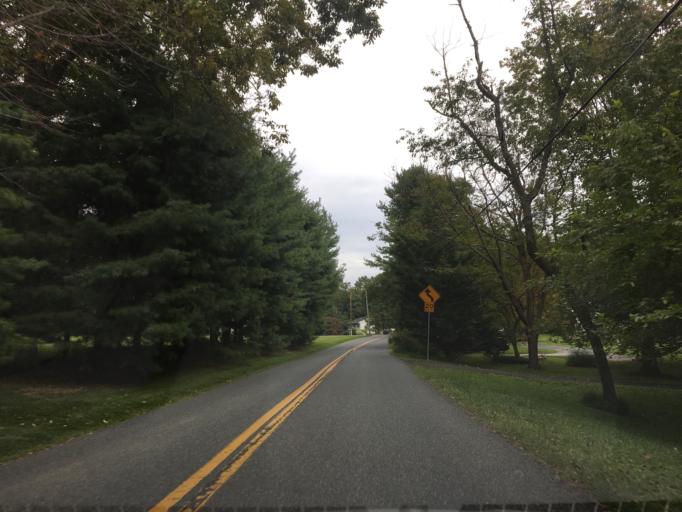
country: US
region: Maryland
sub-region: Baltimore County
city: Hunt Valley
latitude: 39.5059
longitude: -76.5761
